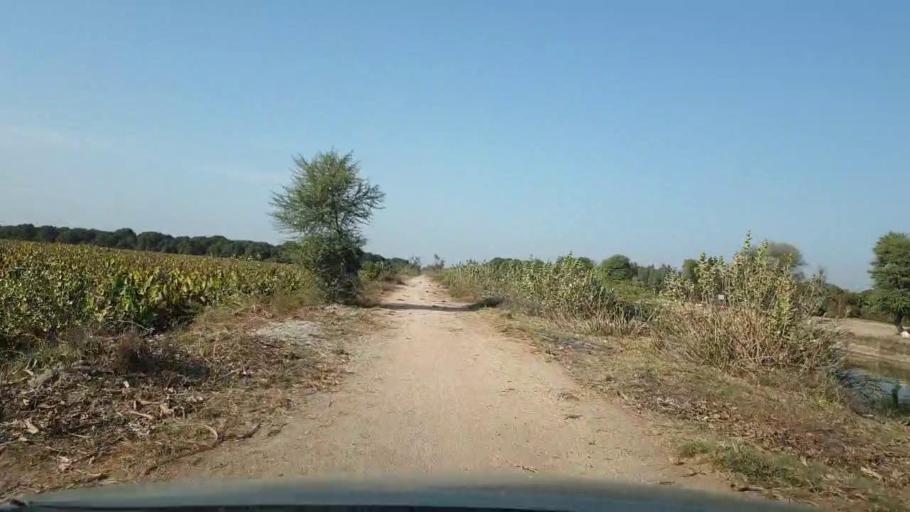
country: PK
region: Sindh
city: Tando Adam
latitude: 25.6024
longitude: 68.6252
